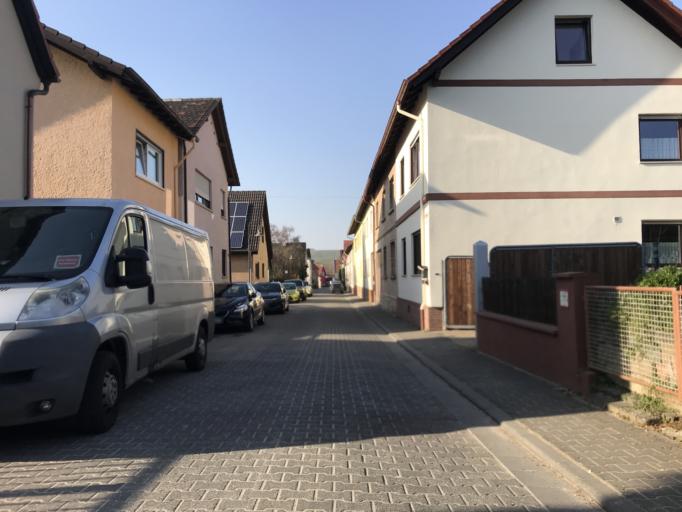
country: DE
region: Rheinland-Pfalz
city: Stadecken-Elsheim
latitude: 49.9075
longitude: 8.1359
